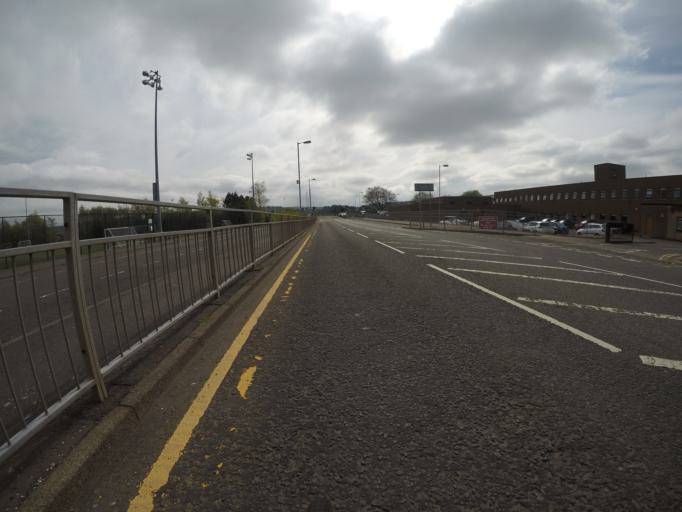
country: GB
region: Scotland
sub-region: East Renfrewshire
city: Newton Mearns
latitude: 55.7693
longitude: -4.3060
